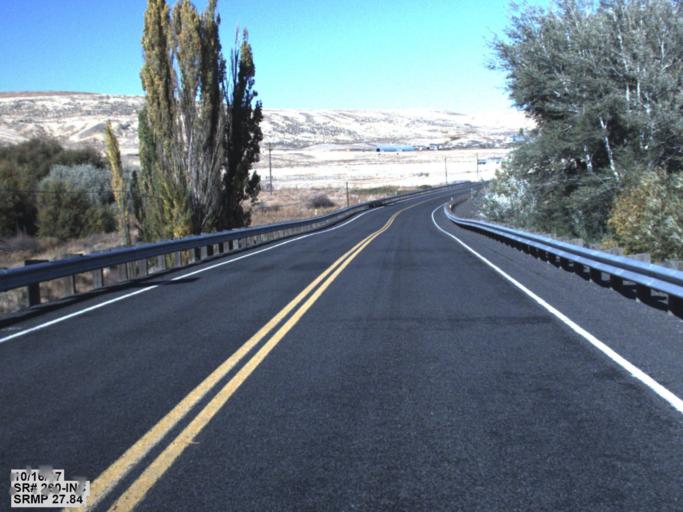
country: US
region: Washington
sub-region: Franklin County
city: Connell
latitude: 46.6545
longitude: -118.4975
